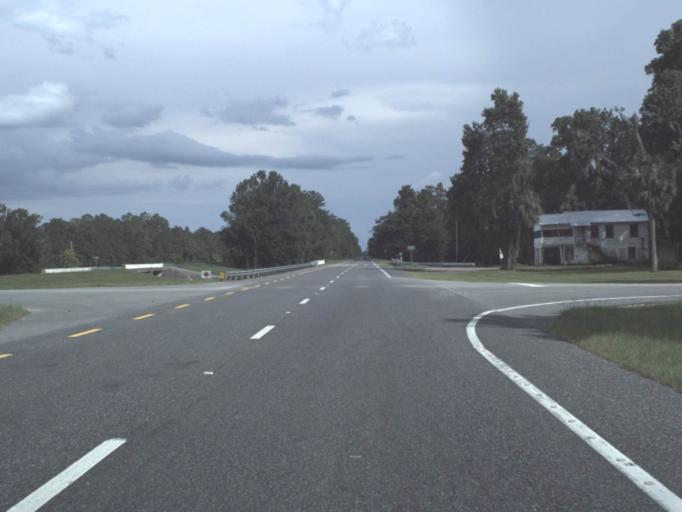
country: US
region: Florida
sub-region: Levy County
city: Bronson
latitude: 29.2770
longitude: -82.7381
